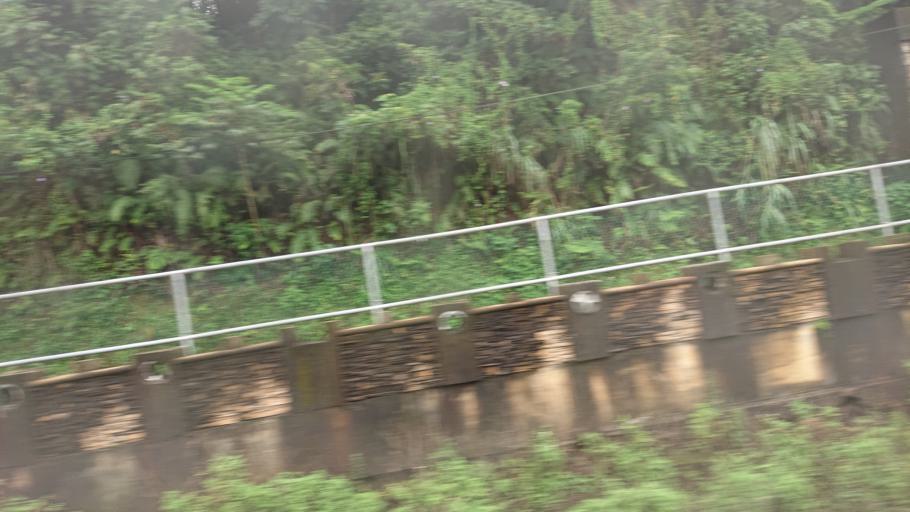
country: TW
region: Taiwan
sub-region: Keelung
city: Keelung
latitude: 25.0831
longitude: 121.7043
